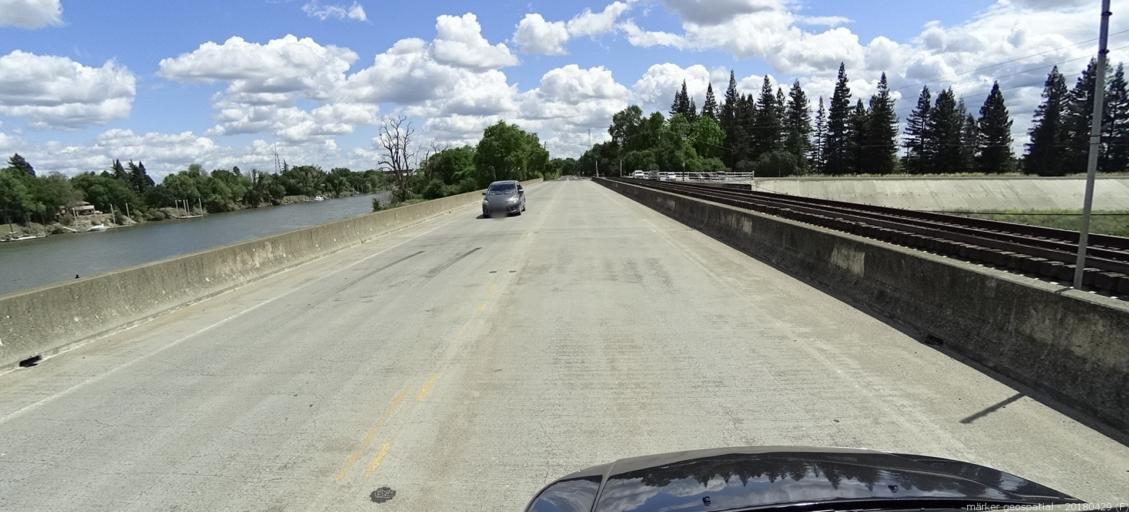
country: US
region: California
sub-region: Yolo County
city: West Sacramento
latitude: 38.6037
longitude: -121.5564
